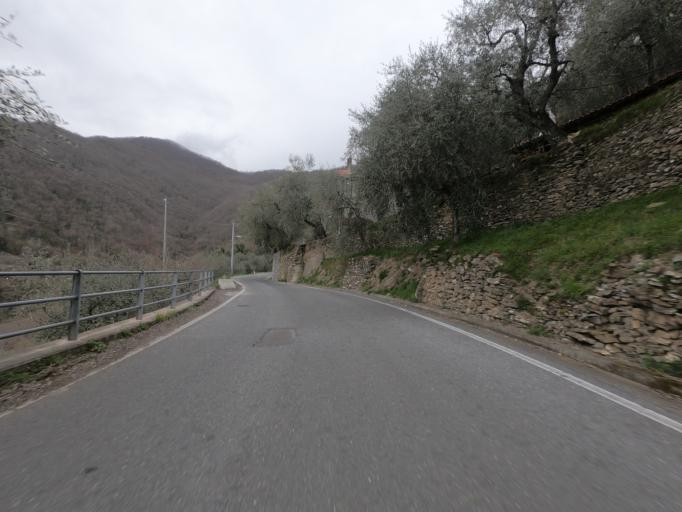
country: IT
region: Liguria
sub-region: Provincia di Savona
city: Testico
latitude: 44.0298
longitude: 8.0199
